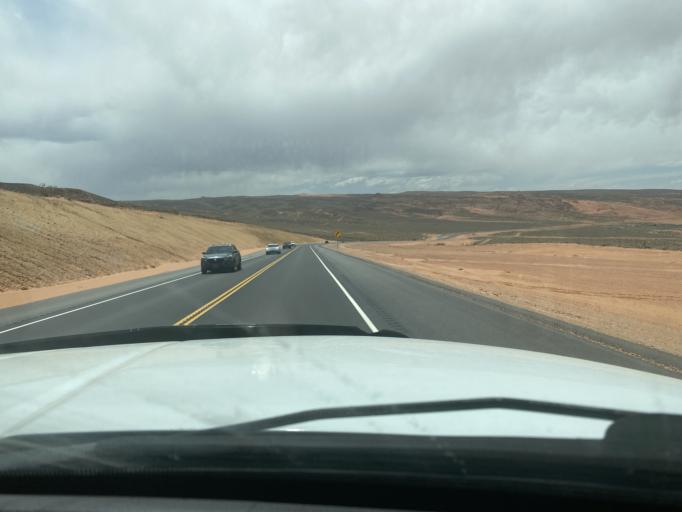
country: US
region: Utah
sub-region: Washington County
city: Hurricane
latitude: 37.1063
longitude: -113.3470
